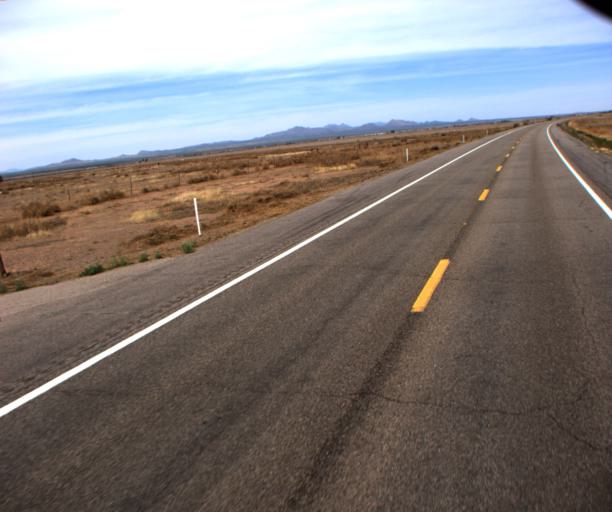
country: US
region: Arizona
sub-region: Cochise County
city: Pirtleville
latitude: 31.5563
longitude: -109.6652
